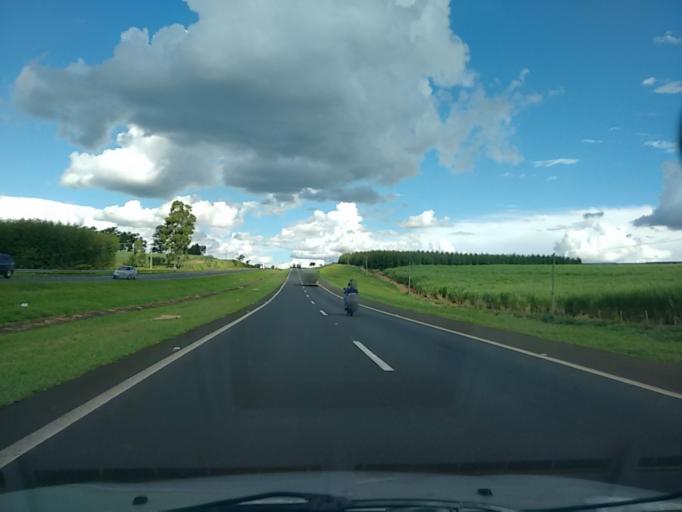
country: BR
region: Sao Paulo
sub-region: Ibate
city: Ibate
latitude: -21.9171
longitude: -48.0393
